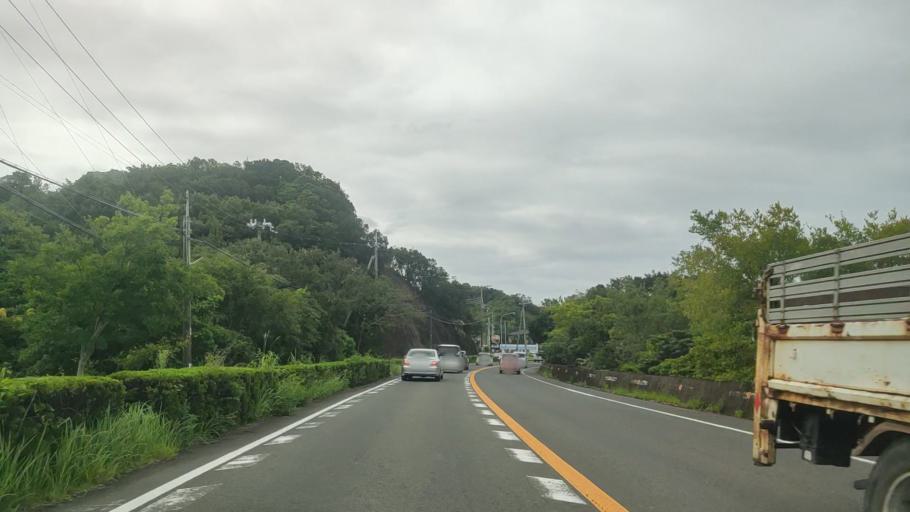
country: JP
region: Wakayama
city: Tanabe
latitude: 33.7034
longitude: 135.3961
